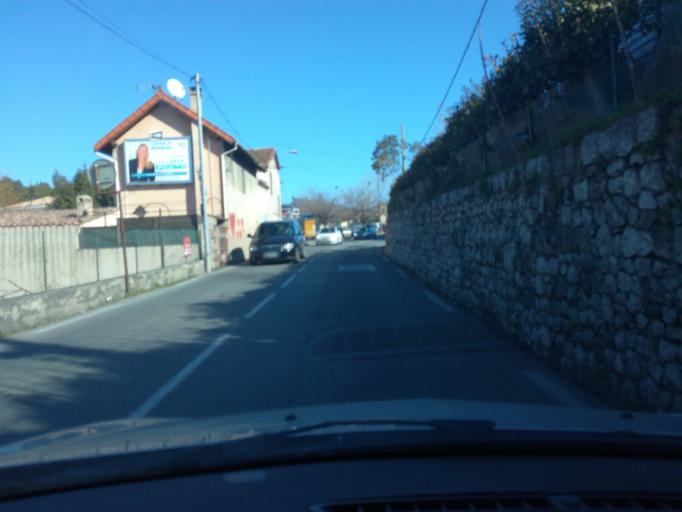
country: FR
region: Provence-Alpes-Cote d'Azur
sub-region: Departement des Alpes-Maritimes
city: Grasse
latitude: 43.6443
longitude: 6.9389
